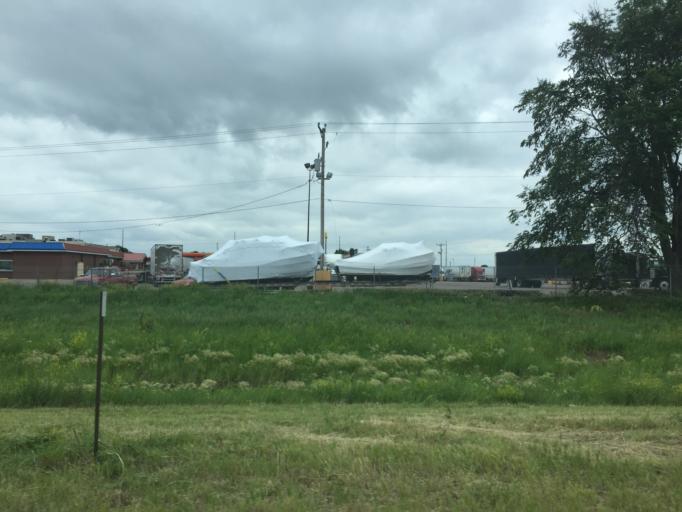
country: US
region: South Dakota
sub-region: Minnehaha County
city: Sioux Falls
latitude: 43.6053
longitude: -96.7128
